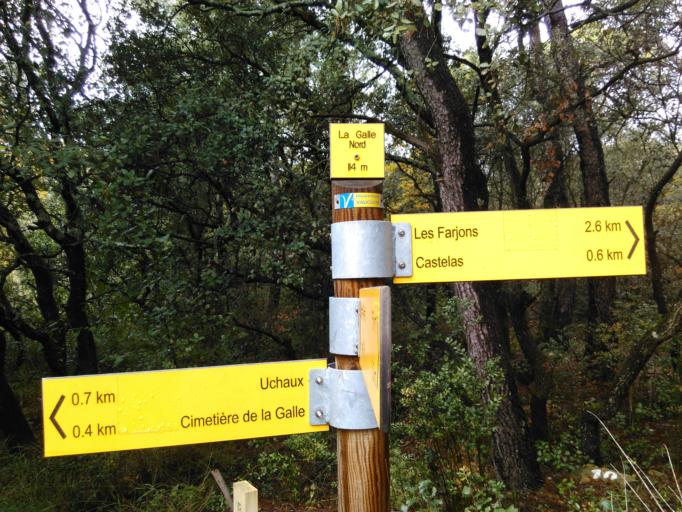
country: FR
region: Provence-Alpes-Cote d'Azur
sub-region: Departement du Vaucluse
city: Uchaux
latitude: 44.2156
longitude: 4.8035
